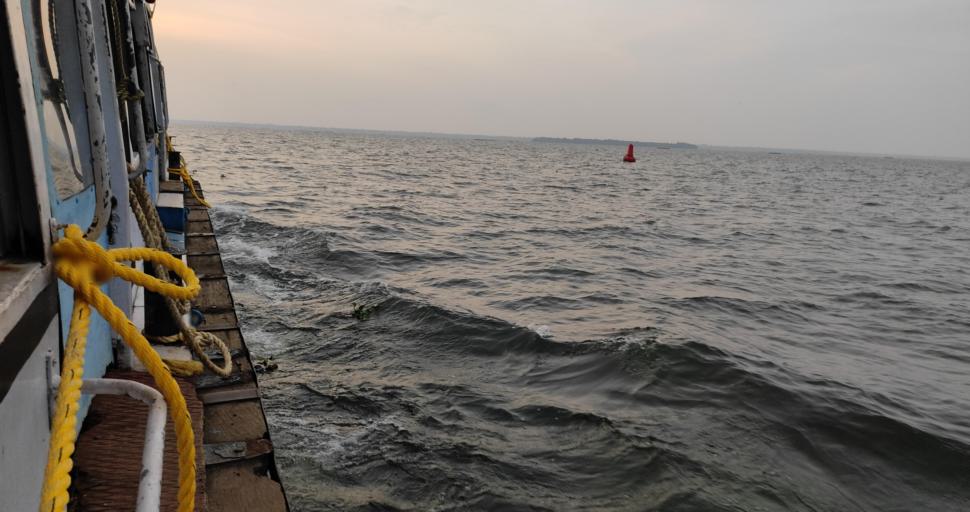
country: IN
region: Kerala
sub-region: Alappuzha
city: Shertallai
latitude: 9.6011
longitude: 76.4056
